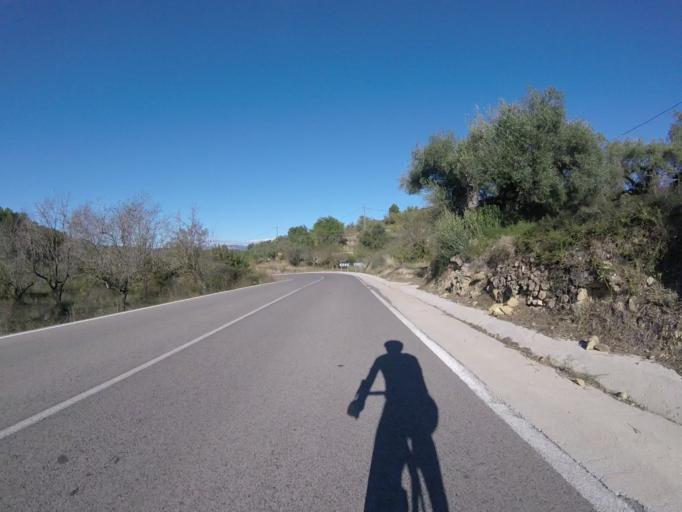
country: ES
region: Valencia
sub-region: Provincia de Castello
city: Cervera del Maestre
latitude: 40.4616
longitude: 0.2606
